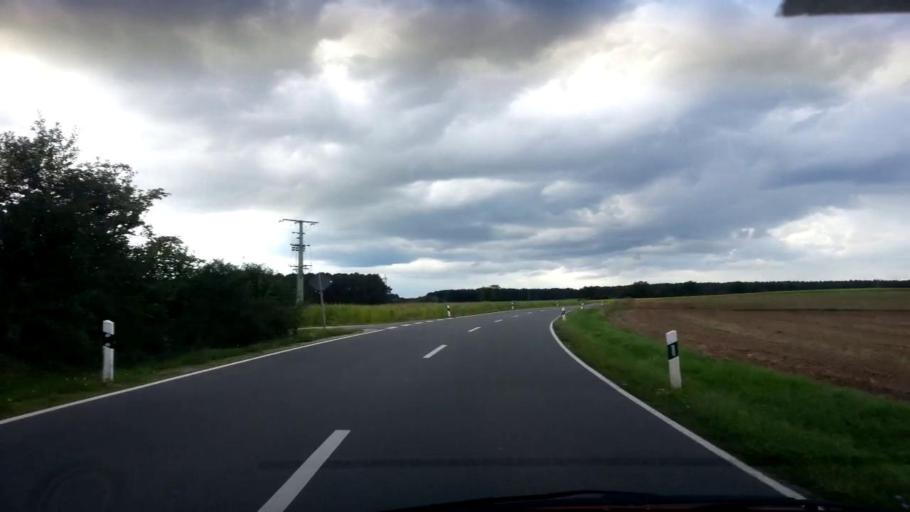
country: DE
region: Bavaria
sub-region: Regierungsbezirk Mittelfranken
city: Hemhofen
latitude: 49.6925
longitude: 10.9611
